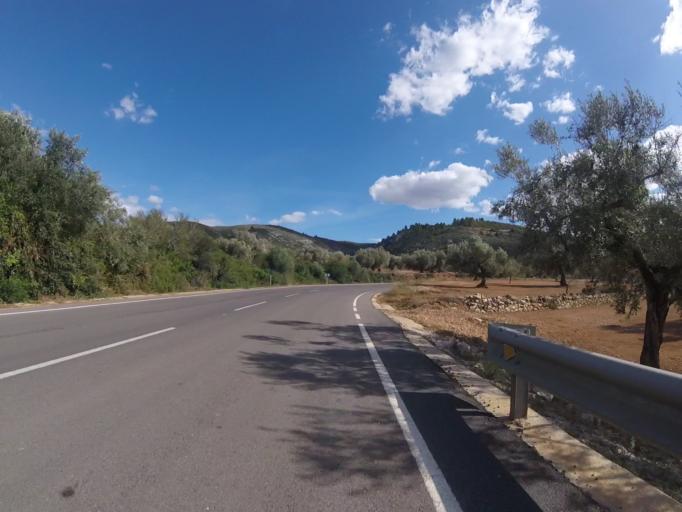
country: ES
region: Valencia
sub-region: Provincia de Castello
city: Cuevas de Vinroma
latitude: 40.3002
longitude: 0.1671
